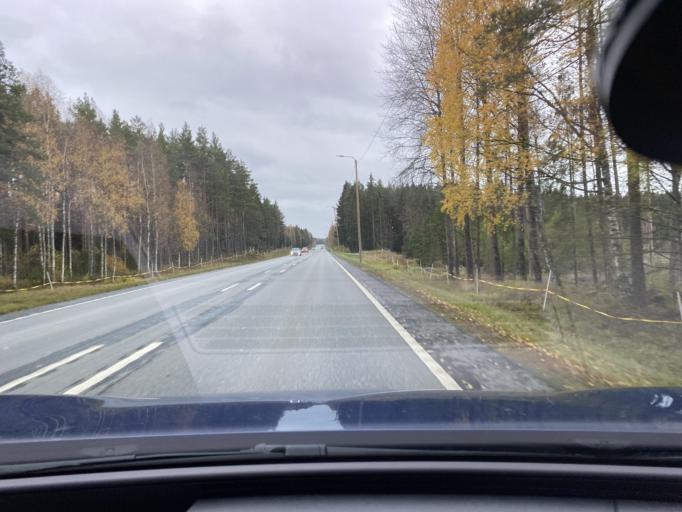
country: FI
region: Varsinais-Suomi
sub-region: Vakka-Suomi
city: Laitila
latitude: 60.9494
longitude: 21.5989
